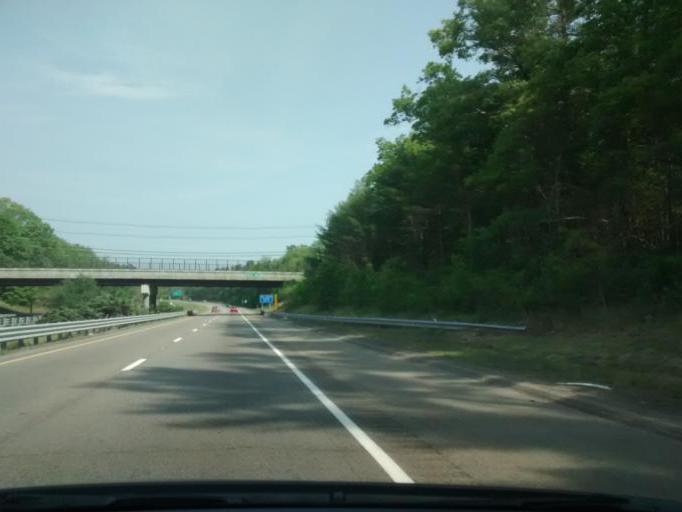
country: US
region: Massachusetts
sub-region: Plymouth County
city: Middleborough Center
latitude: 41.8498
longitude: -70.8598
